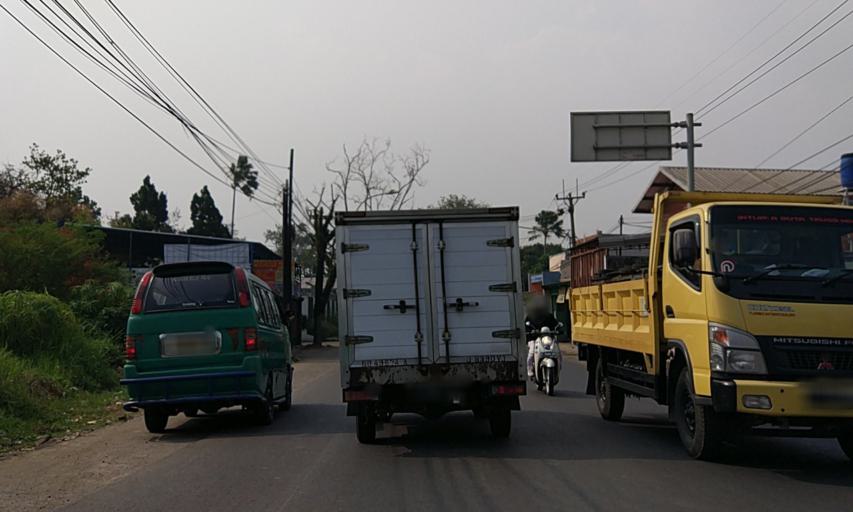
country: ID
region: West Java
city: Margahayukencana
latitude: -6.9921
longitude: 107.5559
